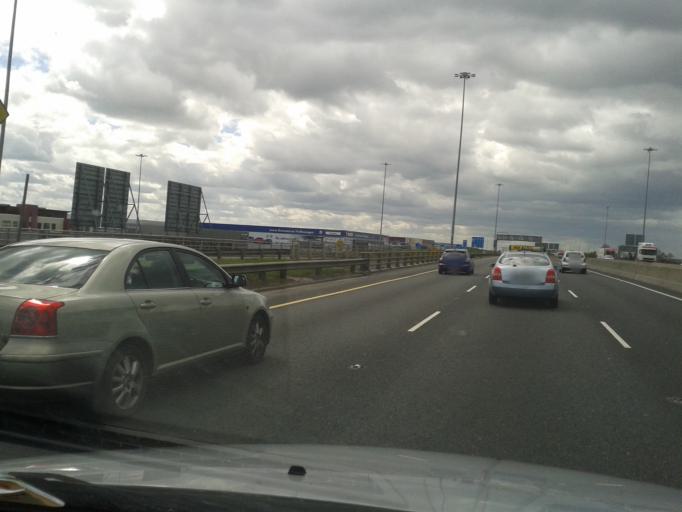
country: IE
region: Leinster
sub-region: Dublin City
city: Finglas
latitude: 53.4043
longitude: -6.3112
